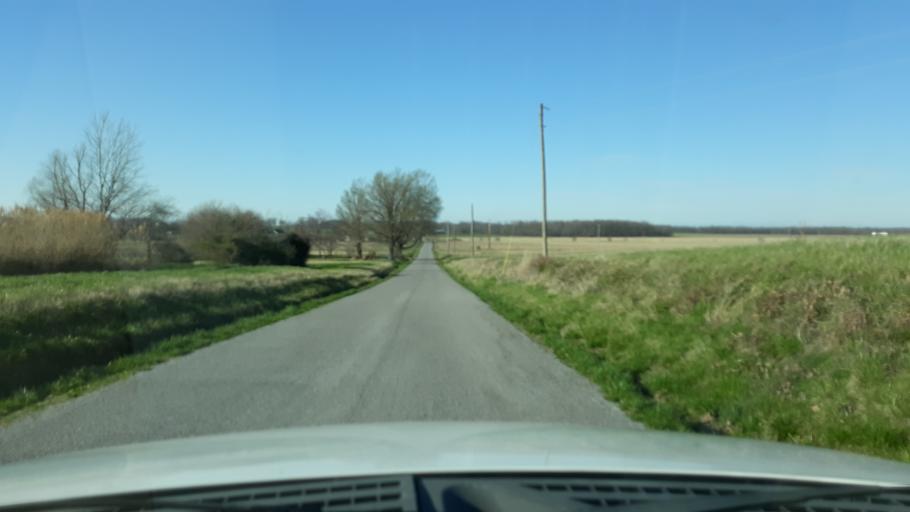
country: US
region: Illinois
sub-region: Saline County
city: Harrisburg
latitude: 37.7647
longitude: -88.5864
